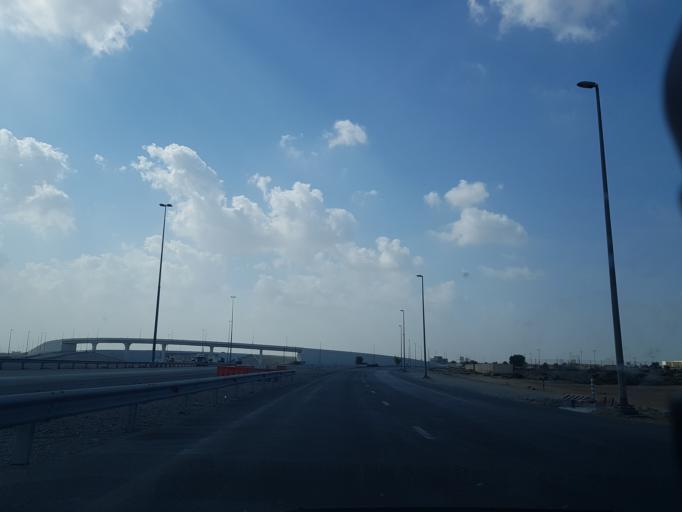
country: AE
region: Ra's al Khaymah
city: Ras al-Khaimah
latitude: 25.8379
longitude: 56.0162
